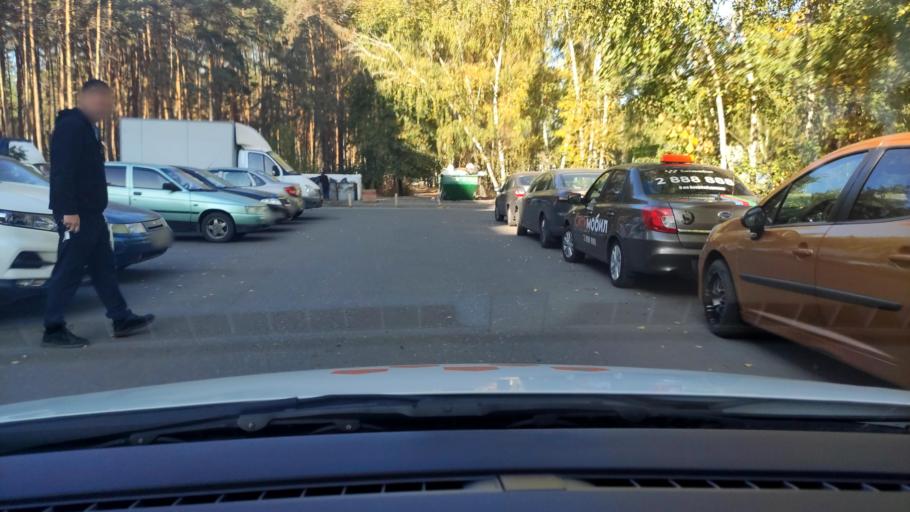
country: RU
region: Voronezj
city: Pridonskoy
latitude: 51.6880
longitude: 39.1068
